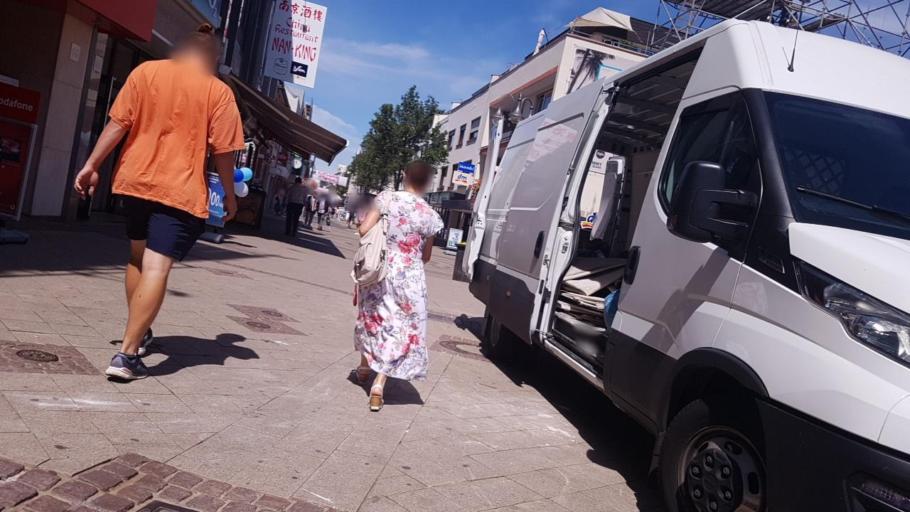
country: DE
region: North Rhine-Westphalia
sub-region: Regierungsbezirk Koln
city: Euskirchen
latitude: 50.6600
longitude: 6.7905
